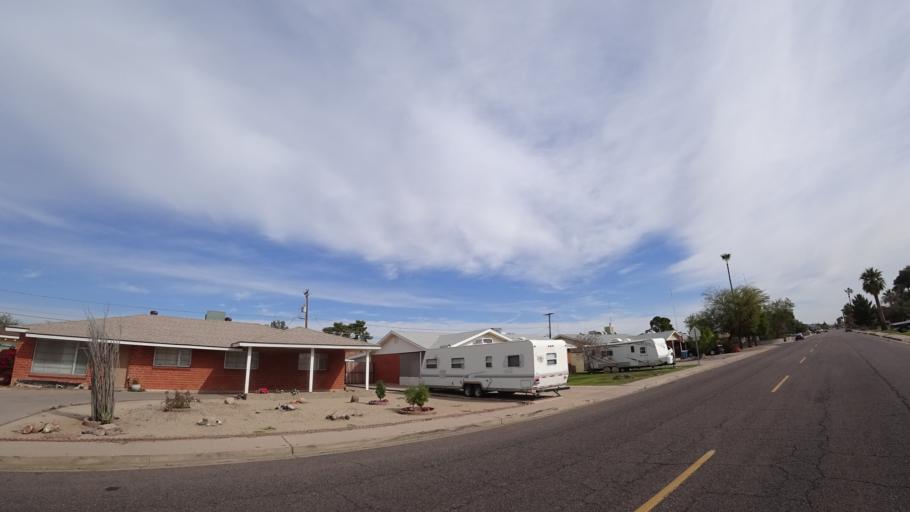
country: US
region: Arizona
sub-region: Maricopa County
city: Glendale
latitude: 33.5312
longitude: -112.1289
